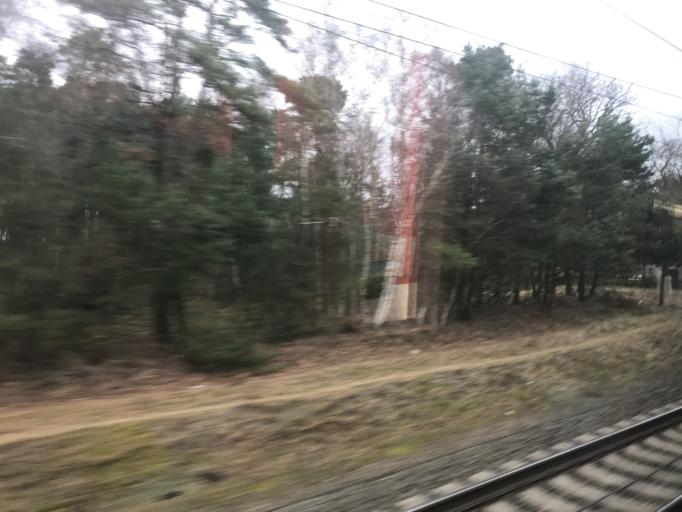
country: DE
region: Lower Saxony
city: Leiferde
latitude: 52.4565
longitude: 10.4363
